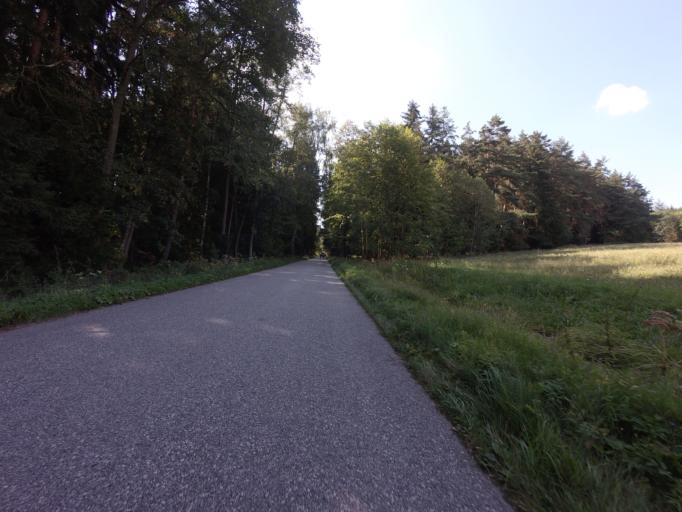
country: CZ
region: Jihocesky
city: Tyn nad Vltavou
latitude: 49.1556
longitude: 14.4364
